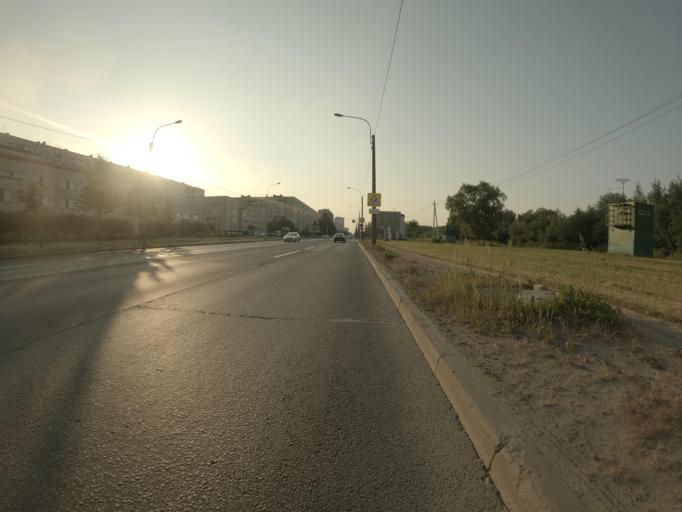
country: RU
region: St.-Petersburg
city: Krasnogvargeisky
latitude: 59.9502
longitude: 30.5011
